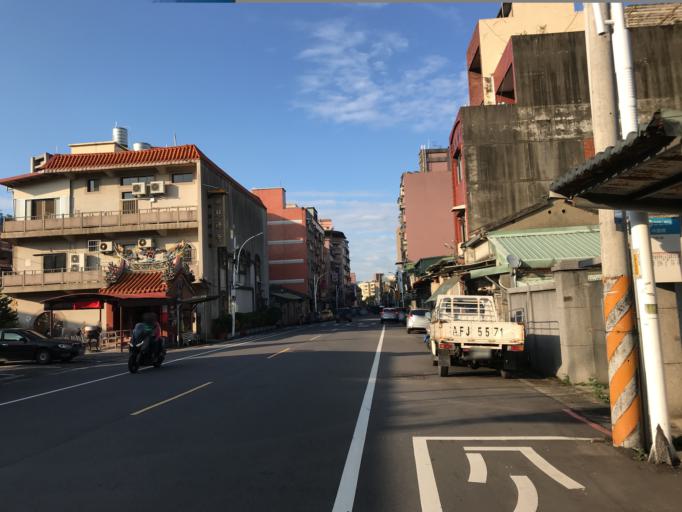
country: TW
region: Taiwan
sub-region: Taoyuan
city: Taoyuan
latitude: 24.9242
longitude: 121.3676
